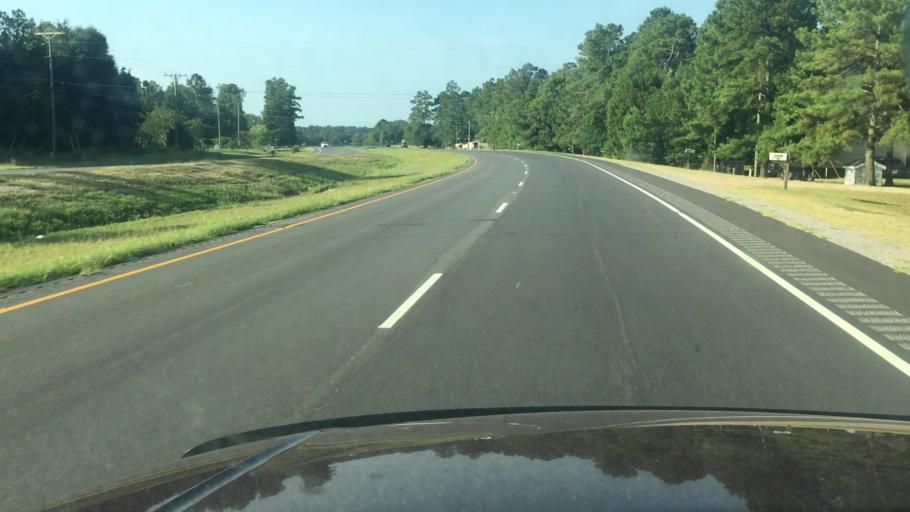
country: US
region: North Carolina
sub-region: Robeson County
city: Saint Pauls
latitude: 34.8682
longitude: -78.8502
